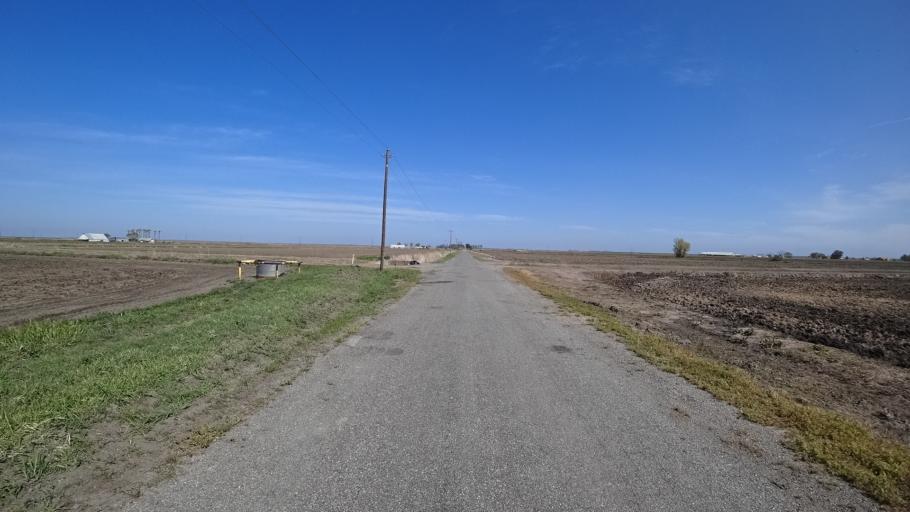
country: US
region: California
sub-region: Glenn County
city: Hamilton City
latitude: 39.6122
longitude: -122.0744
